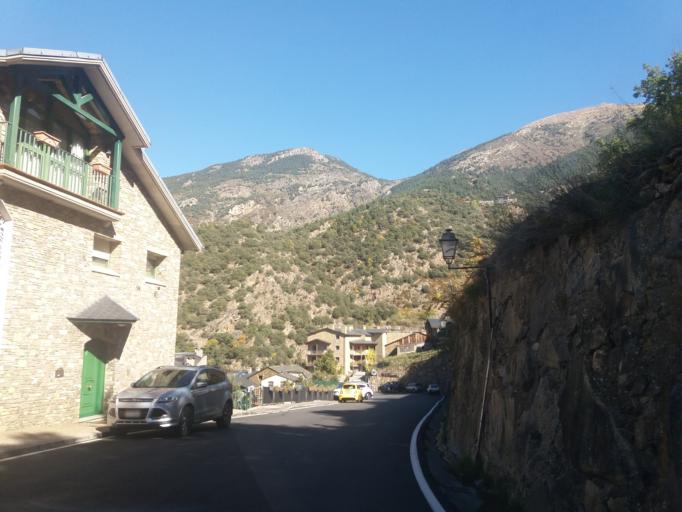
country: AD
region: Sant Julia de Loria
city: Sant Julia de Loria
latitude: 42.4619
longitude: 1.5011
